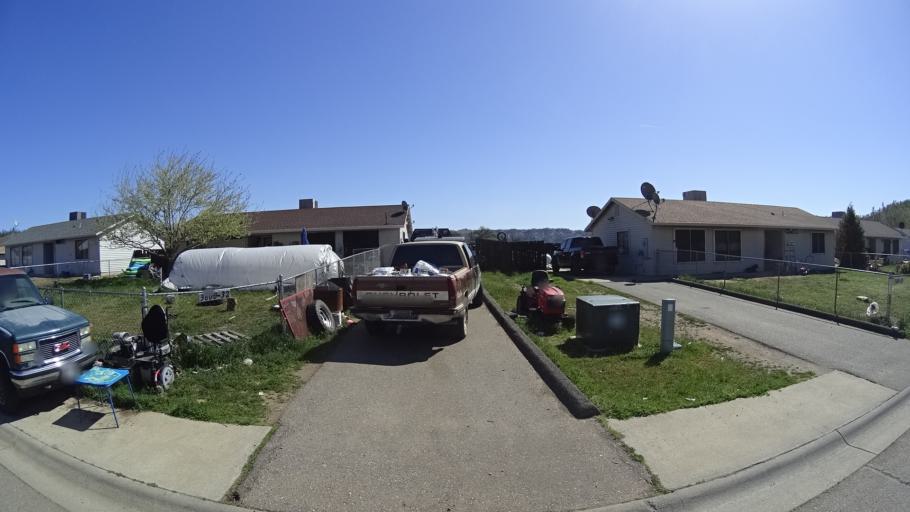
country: US
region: California
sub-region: Glenn County
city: Orland
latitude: 39.6752
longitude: -122.5205
